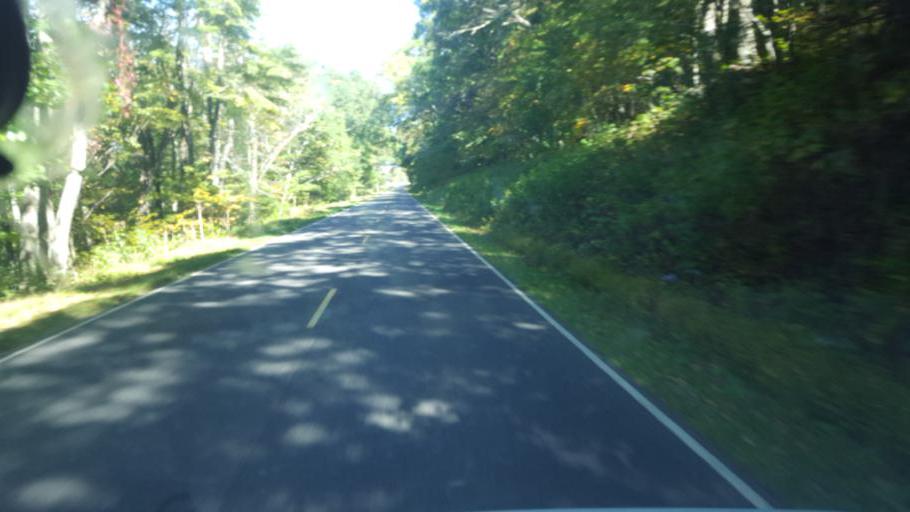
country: US
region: Virginia
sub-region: Page County
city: Stanley
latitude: 38.4742
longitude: -78.4570
